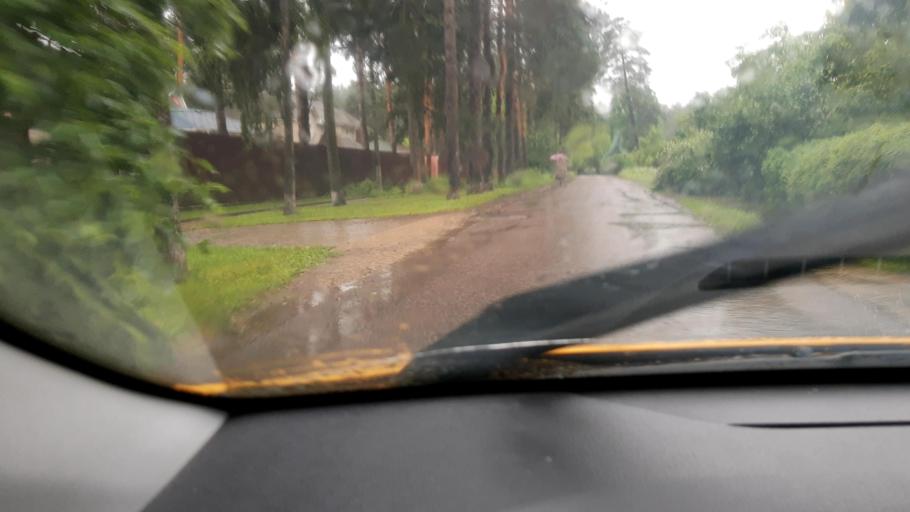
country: RU
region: Moskovskaya
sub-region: Podol'skiy Rayon
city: Podol'sk
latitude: 55.4132
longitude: 37.6141
